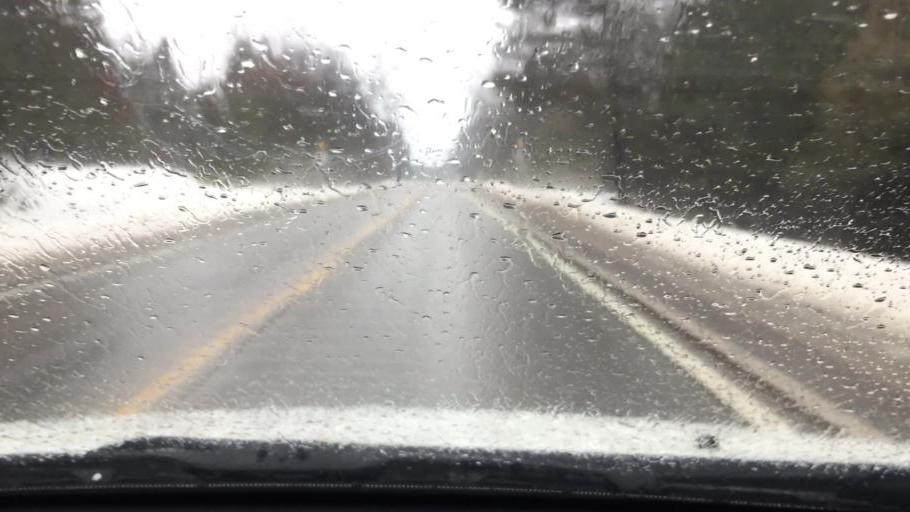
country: US
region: Michigan
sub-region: Charlevoix County
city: Charlevoix
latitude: 45.2522
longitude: -85.1848
